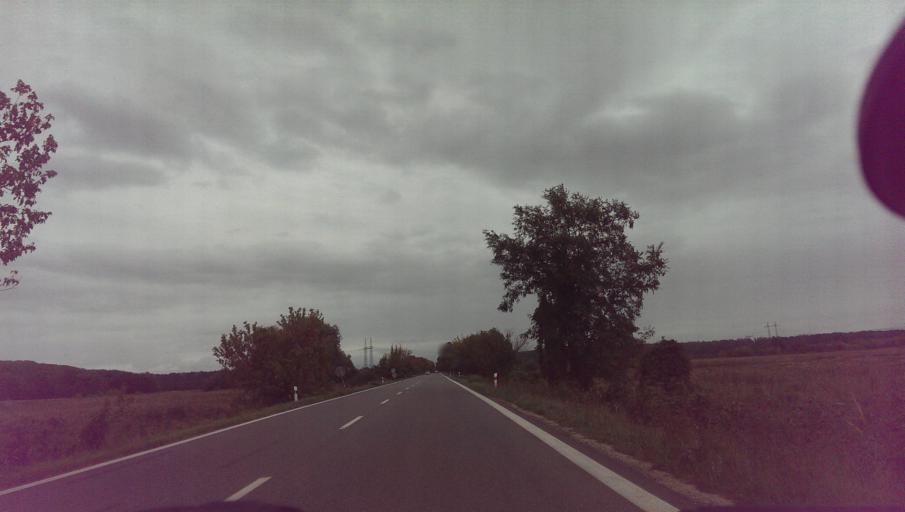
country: CZ
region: South Moravian
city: Moravsky Pisek
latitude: 48.9785
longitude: 17.3213
